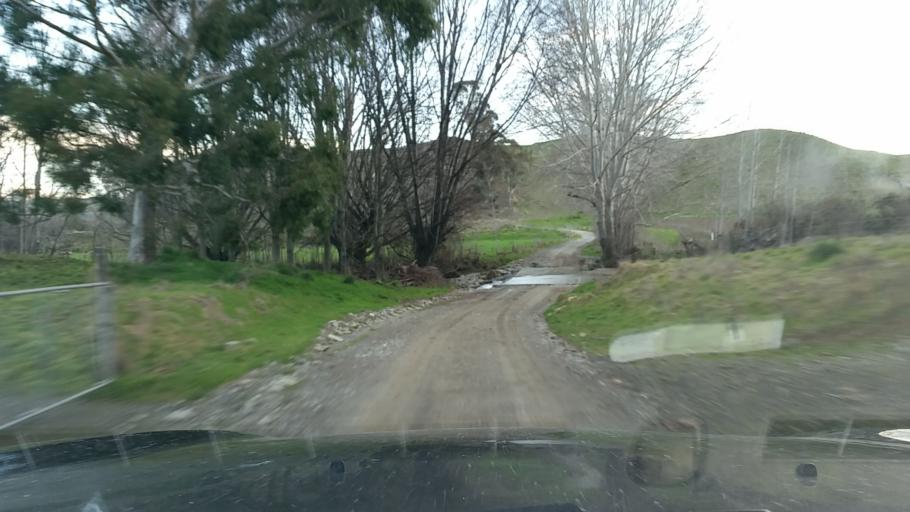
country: NZ
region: Marlborough
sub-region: Marlborough District
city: Blenheim
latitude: -41.5076
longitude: 173.5919
